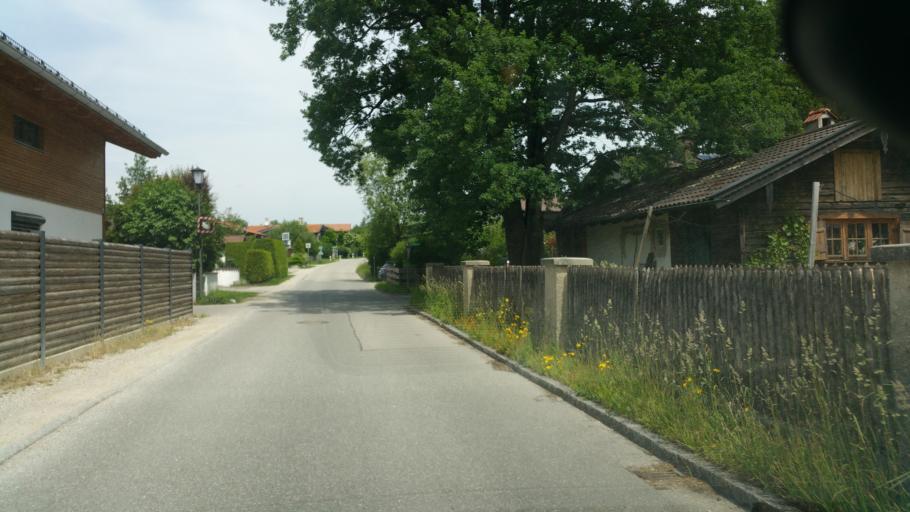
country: DE
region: Bavaria
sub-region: Upper Bavaria
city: Aschau im Chiemgau
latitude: 47.7913
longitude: 12.3256
